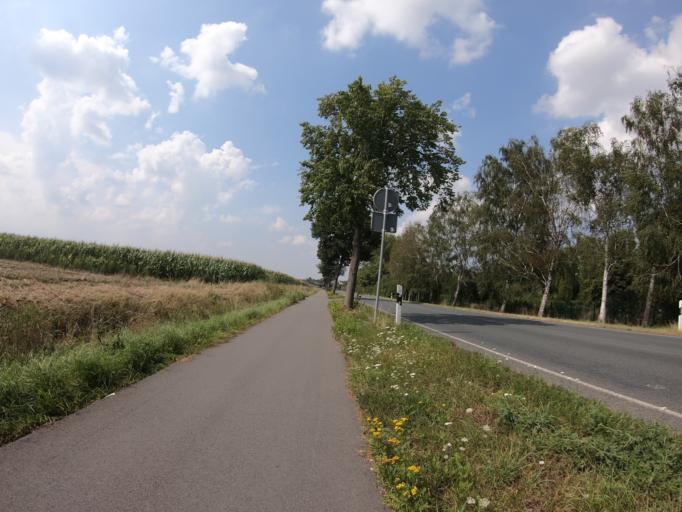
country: DE
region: Lower Saxony
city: Sickte
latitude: 52.2137
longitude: 10.6523
